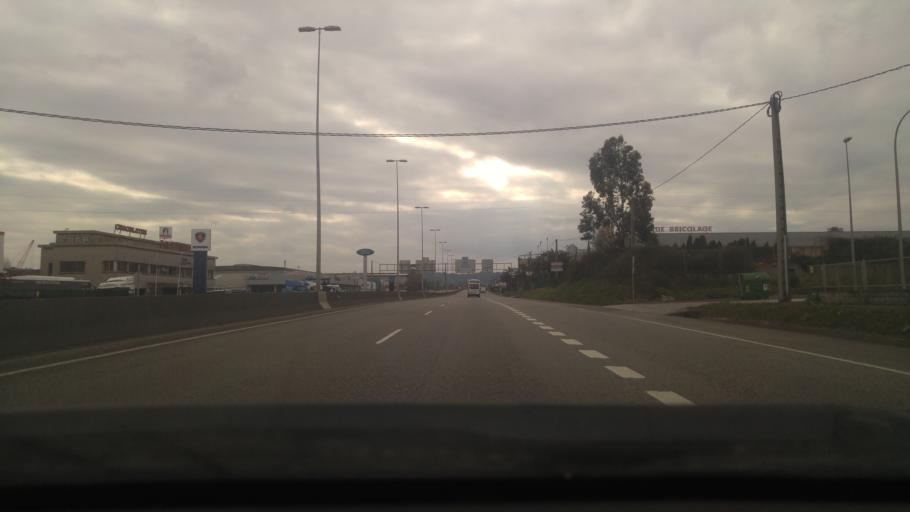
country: ES
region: Asturias
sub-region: Province of Asturias
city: Natahoyo
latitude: 43.5057
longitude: -5.6982
